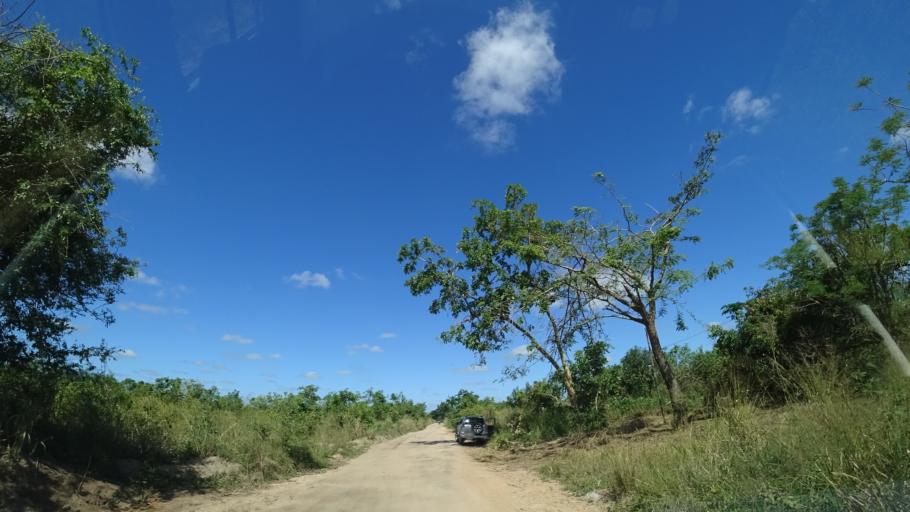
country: MZ
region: Sofala
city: Dondo
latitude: -19.3234
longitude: 34.6920
